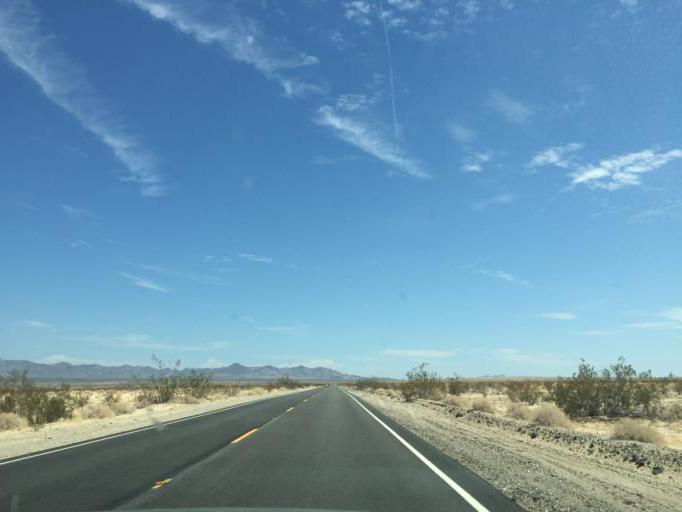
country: US
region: California
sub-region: Riverside County
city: Mesa Verde
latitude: 34.0985
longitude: -115.0149
